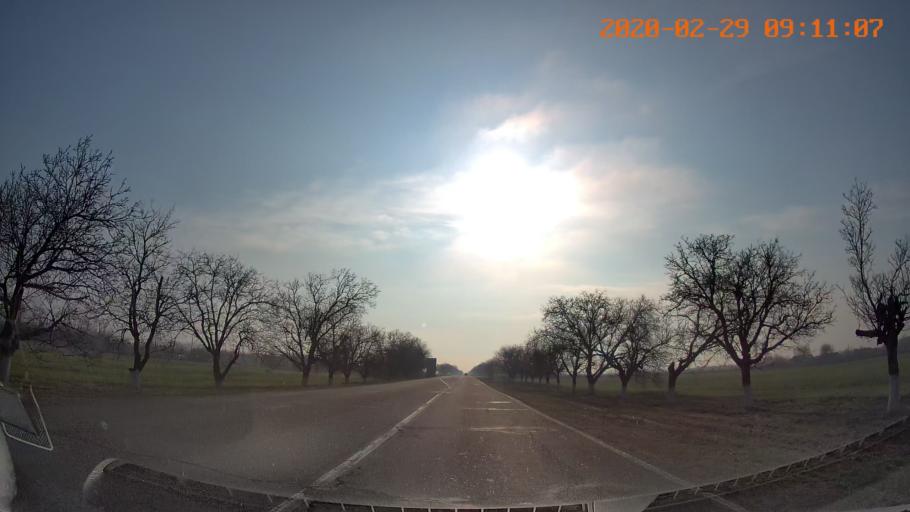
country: MD
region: Telenesti
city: Slobozia
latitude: 46.8380
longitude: 29.7940
